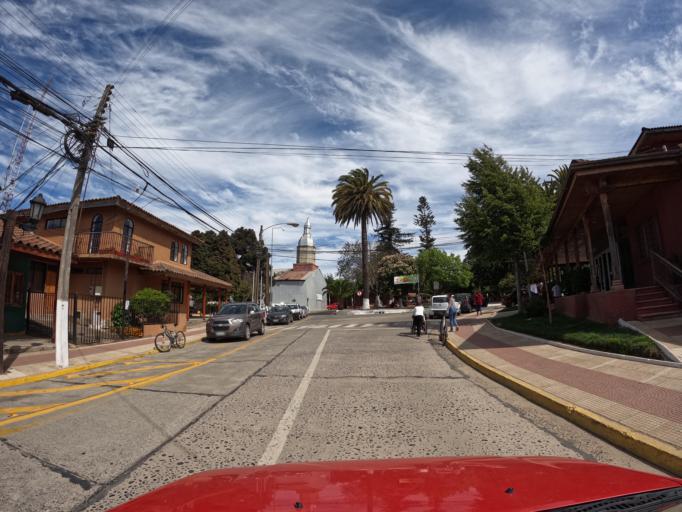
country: CL
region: Maule
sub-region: Provincia de Talca
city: Constitucion
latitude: -35.0933
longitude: -72.0181
